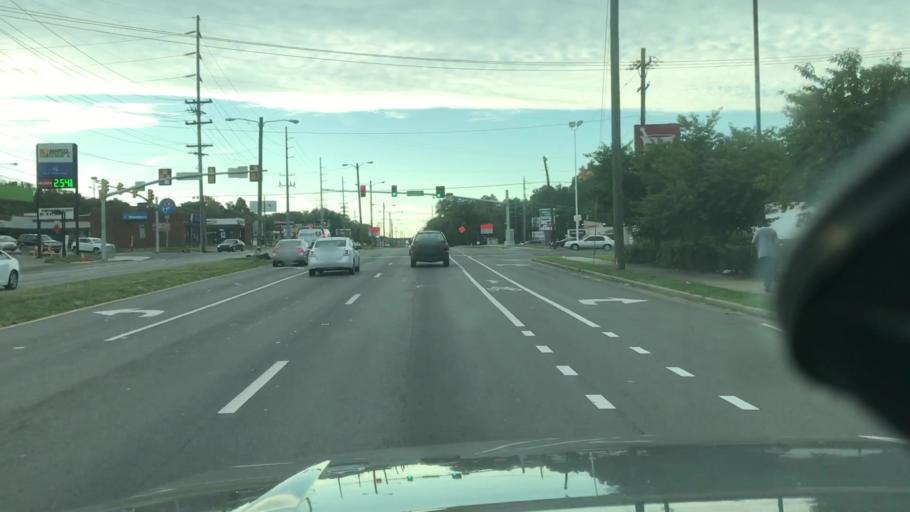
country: US
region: Tennessee
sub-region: Davidson County
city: Oak Hill
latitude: 36.1271
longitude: -86.7118
